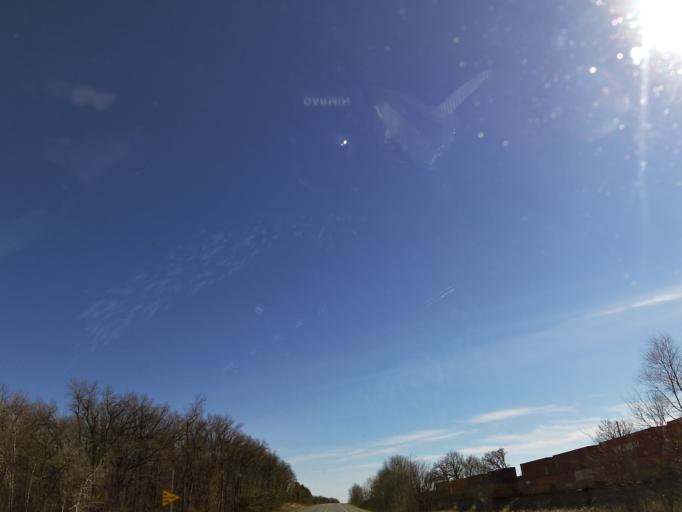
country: US
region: Minnesota
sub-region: Wright County
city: Buffalo
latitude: 45.1324
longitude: -93.8229
